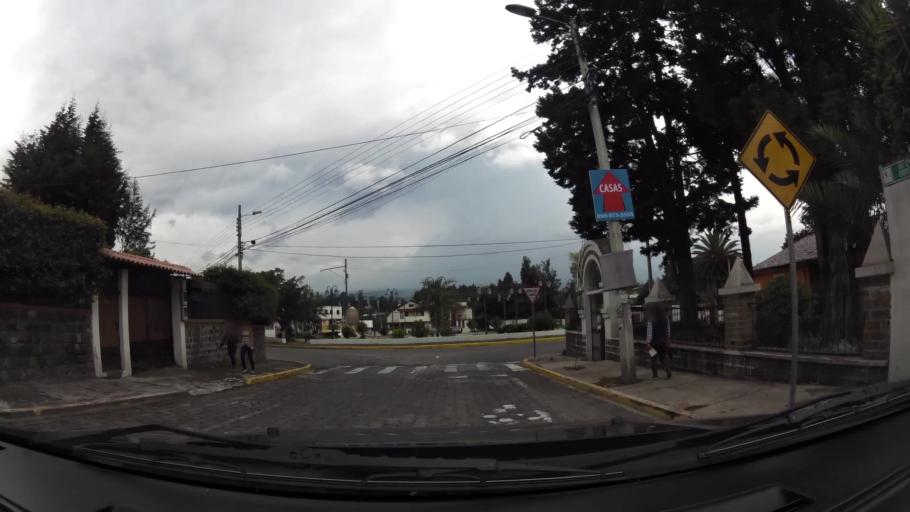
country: EC
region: Pichincha
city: Sangolqui
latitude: -0.3350
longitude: -78.4520
